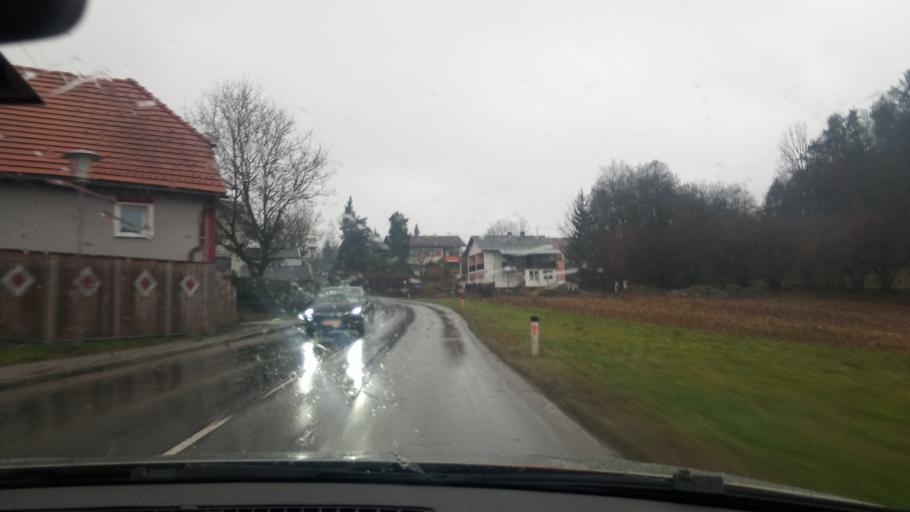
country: AT
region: Carinthia
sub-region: Politischer Bezirk Klagenfurt Land
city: Kottmannsdorf
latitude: 46.5873
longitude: 14.2375
